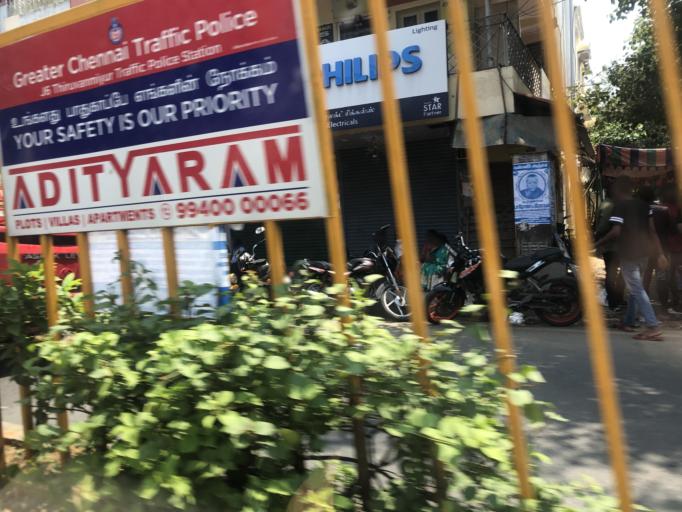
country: IN
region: Tamil Nadu
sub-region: Chennai
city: Gandhi Nagar
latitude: 12.9961
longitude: 80.2558
